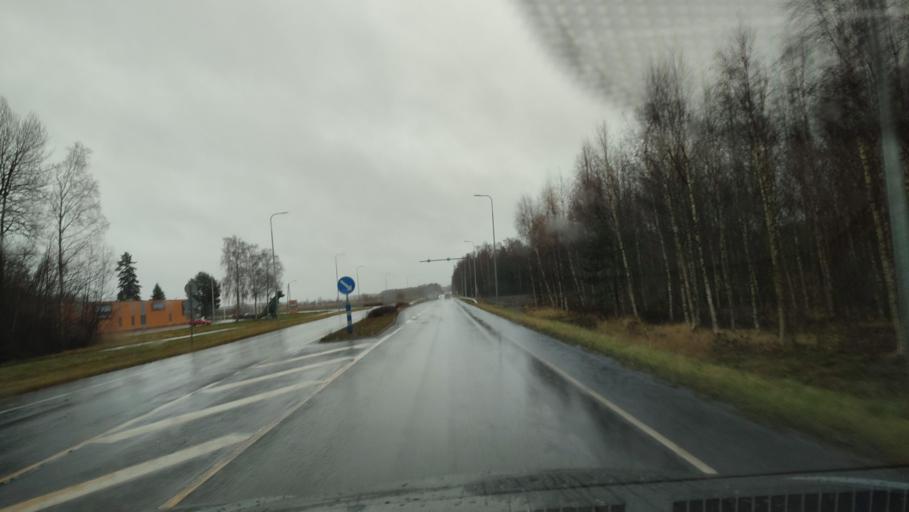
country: FI
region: Ostrobothnia
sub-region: Vaasa
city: Ristinummi
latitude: 63.0495
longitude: 21.7272
